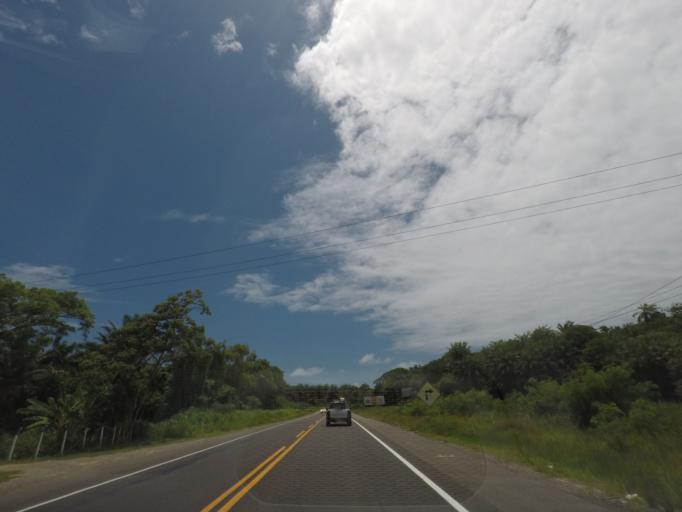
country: BR
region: Bahia
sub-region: Itaparica
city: Itaparica
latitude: -12.9813
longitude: -38.6322
